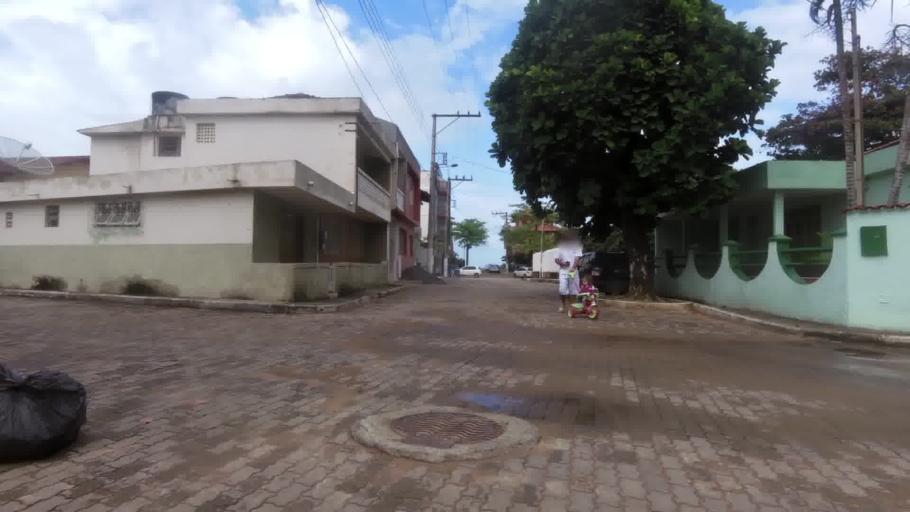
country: BR
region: Espirito Santo
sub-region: Piuma
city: Piuma
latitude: -20.8300
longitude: -40.6913
